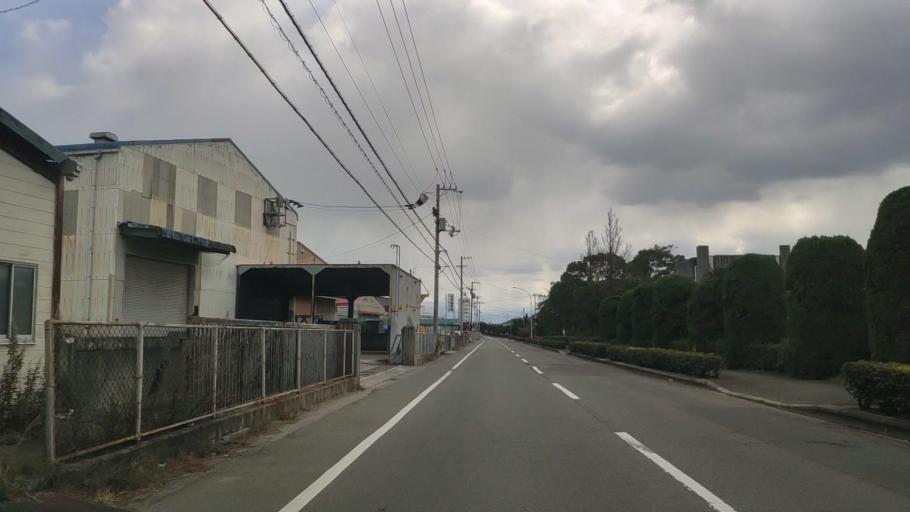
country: JP
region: Ehime
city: Saijo
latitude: 34.0548
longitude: 133.0218
